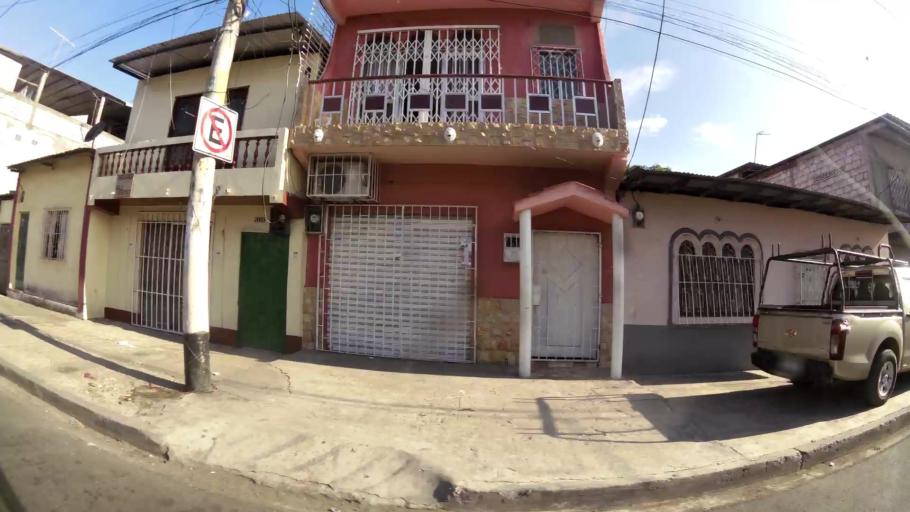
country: EC
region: Guayas
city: Guayaquil
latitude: -2.2221
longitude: -79.9203
